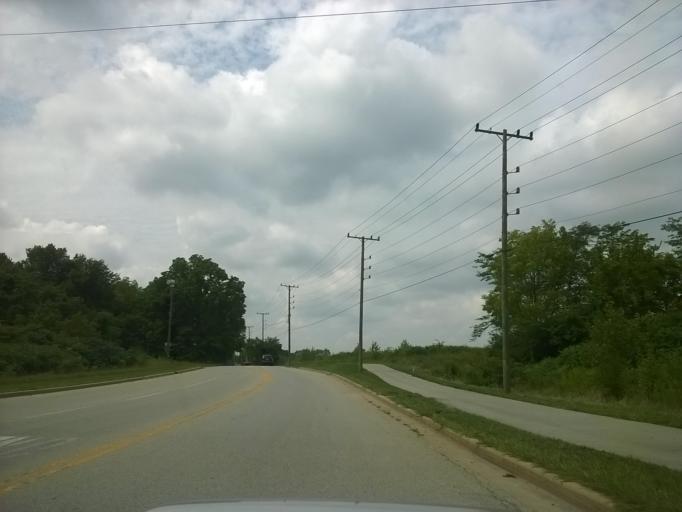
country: US
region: Indiana
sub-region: Hamilton County
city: Carmel
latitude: 39.9413
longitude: -86.0750
